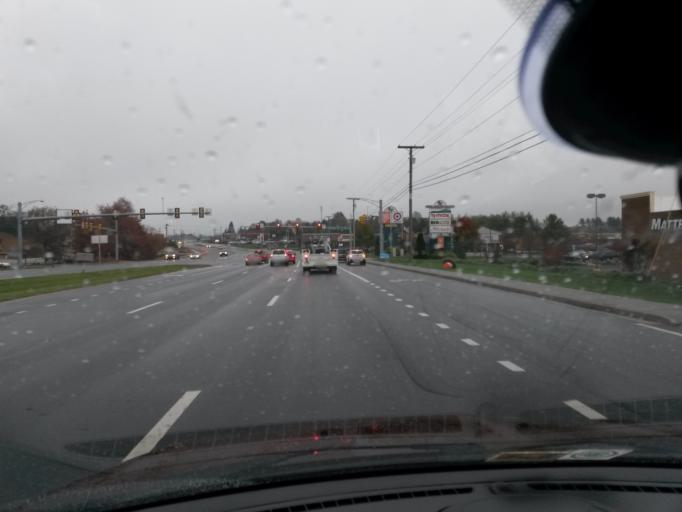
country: US
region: Virginia
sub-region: Montgomery County
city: Merrimac
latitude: 37.1610
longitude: -80.4225
